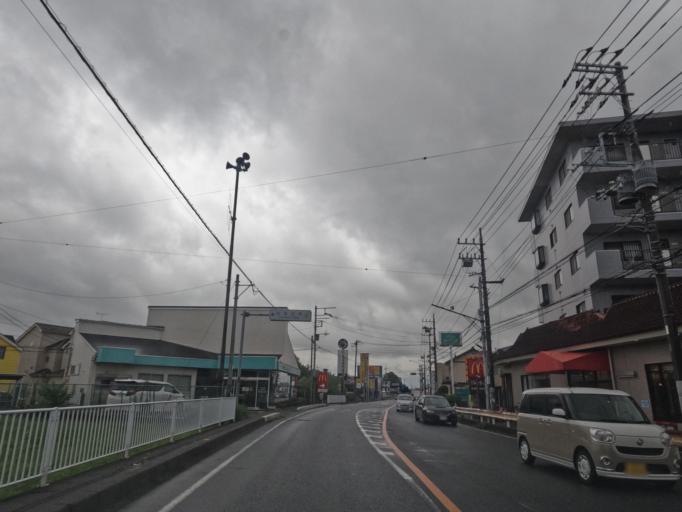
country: JP
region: Saitama
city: Yono
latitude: 35.8599
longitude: 139.6755
